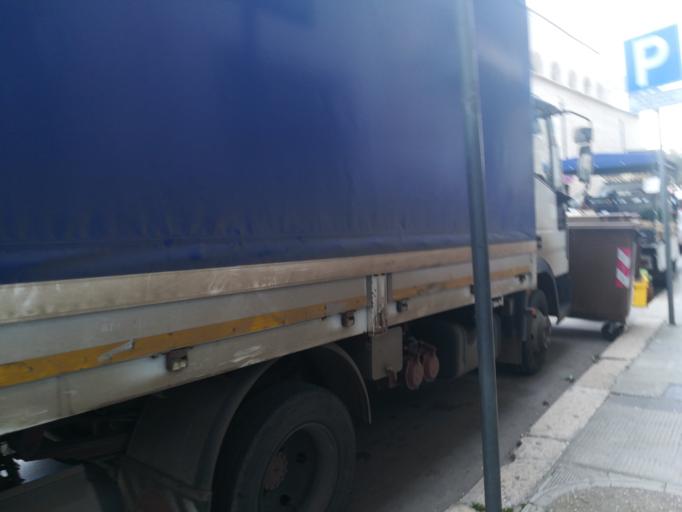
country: IT
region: Apulia
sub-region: Provincia di Bari
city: Bitonto
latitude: 41.1096
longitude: 16.6918
